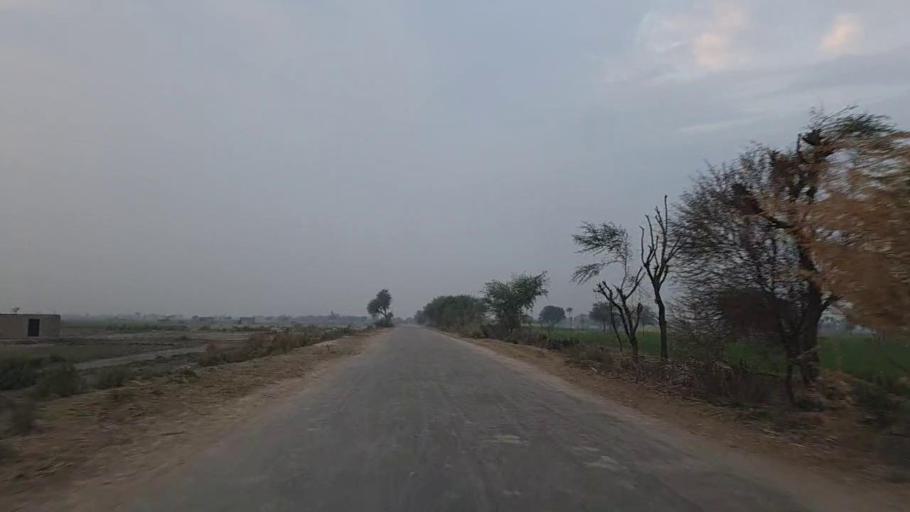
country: PK
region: Sindh
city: Jam Sahib
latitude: 26.3198
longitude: 68.5579
